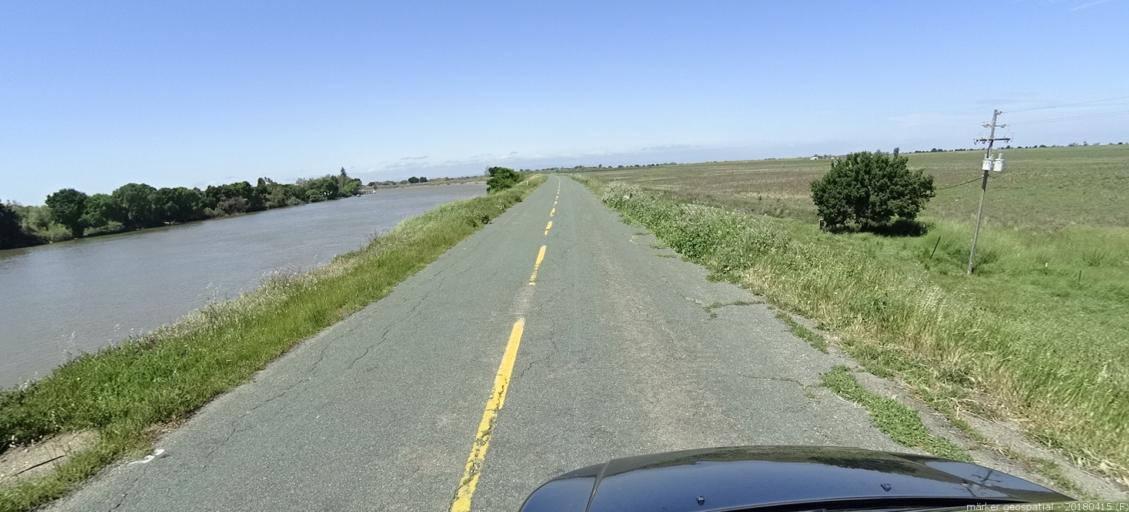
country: US
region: California
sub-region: Solano County
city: Rio Vista
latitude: 38.1707
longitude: -121.6309
